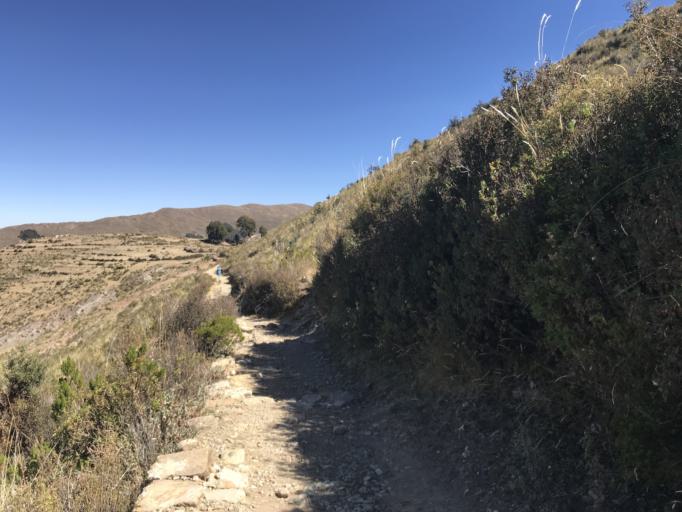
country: BO
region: La Paz
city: Yumani
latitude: -16.0312
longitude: -69.1579
